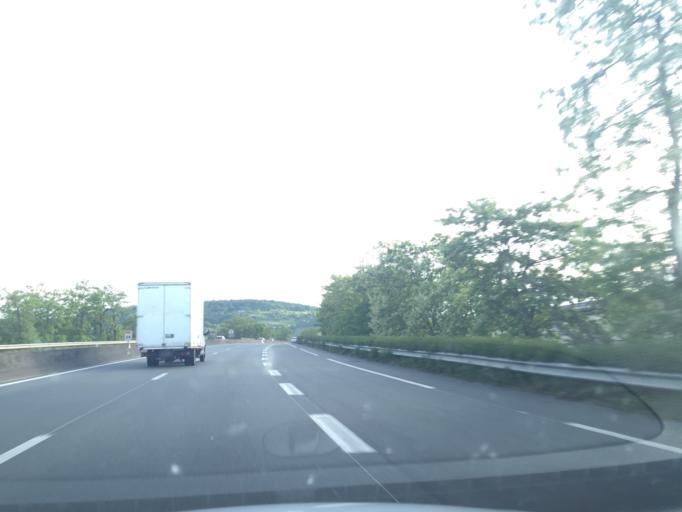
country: FR
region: Auvergne
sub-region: Departement du Puy-de-Dome
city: Menetrol
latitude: 45.8783
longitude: 3.1272
